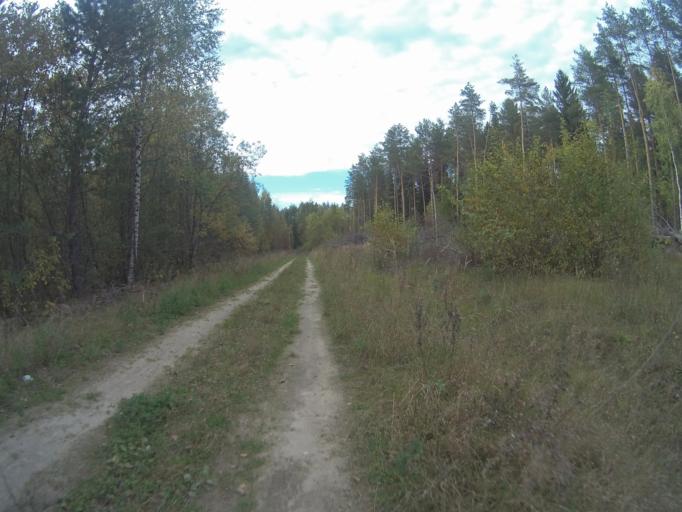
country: RU
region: Vladimir
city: Golovino
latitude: 55.9662
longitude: 40.4204
